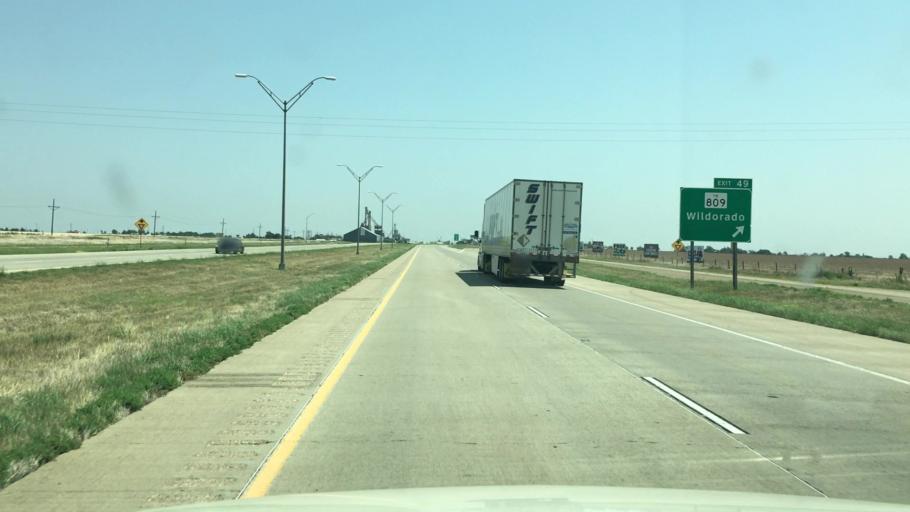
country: US
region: Texas
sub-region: Potter County
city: Bushland
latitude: 35.2098
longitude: -102.2208
